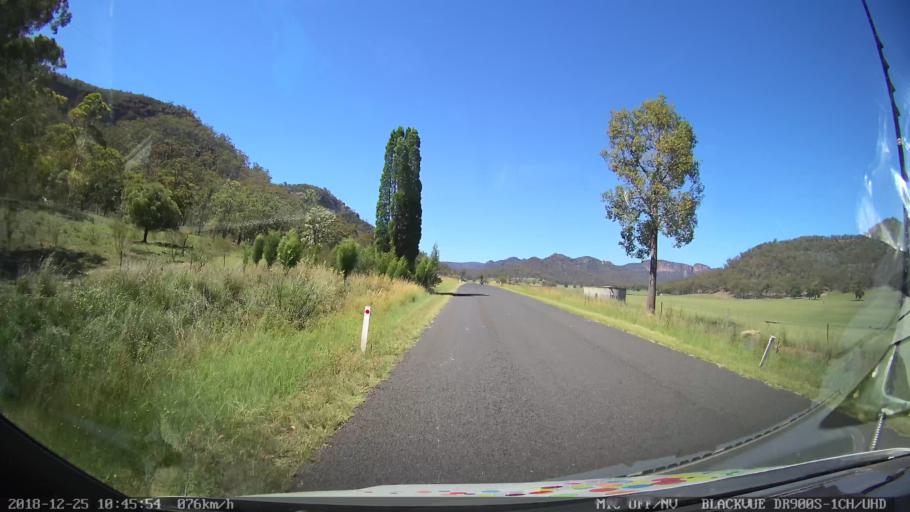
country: AU
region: New South Wales
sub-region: Upper Hunter Shire
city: Merriwa
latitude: -32.4383
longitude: 150.2876
